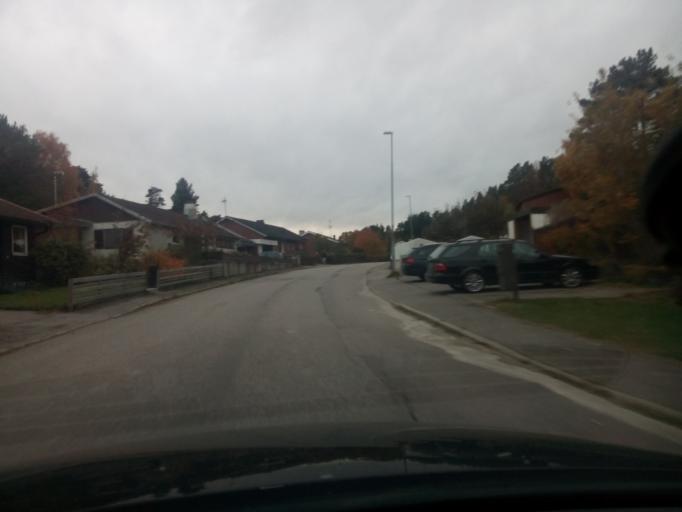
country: SE
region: Soedermanland
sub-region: Nykopings Kommun
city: Nykoping
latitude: 58.7508
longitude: 17.0430
